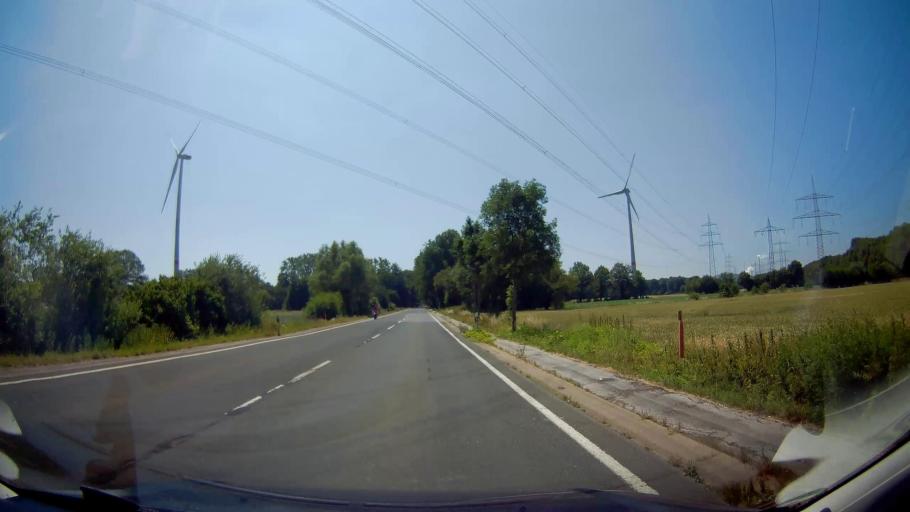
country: DE
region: North Rhine-Westphalia
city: Marl
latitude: 51.6448
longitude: 7.0445
